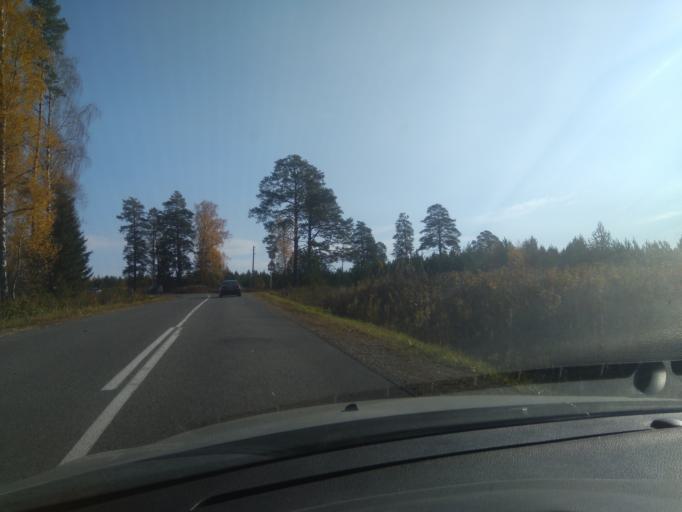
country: RU
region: Sverdlovsk
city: Mikhaylovsk
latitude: 56.5321
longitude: 59.2093
